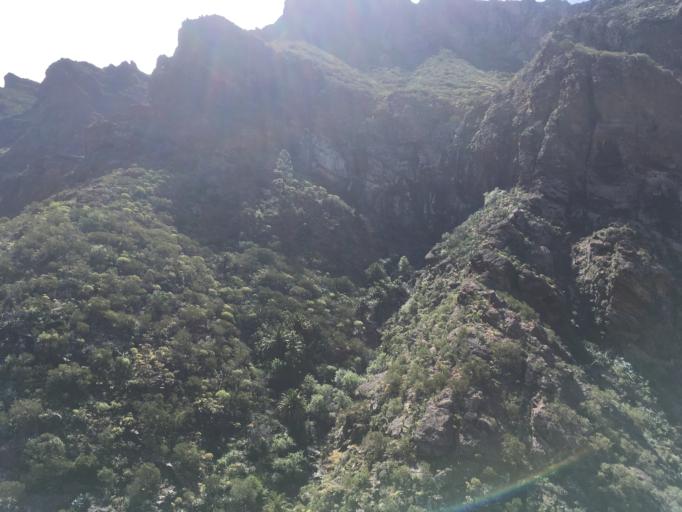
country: ES
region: Canary Islands
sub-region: Provincia de Santa Cruz de Tenerife
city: Santiago del Teide
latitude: 28.3019
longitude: -16.8377
